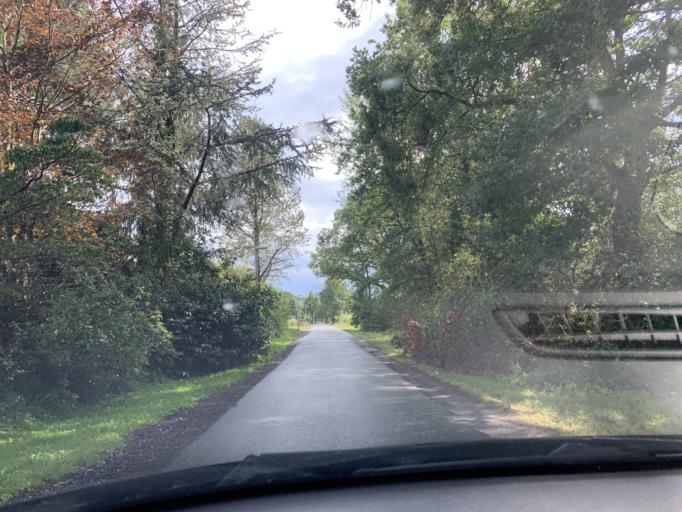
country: DE
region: Lower Saxony
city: Westerstede
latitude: 53.2582
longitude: 7.9016
